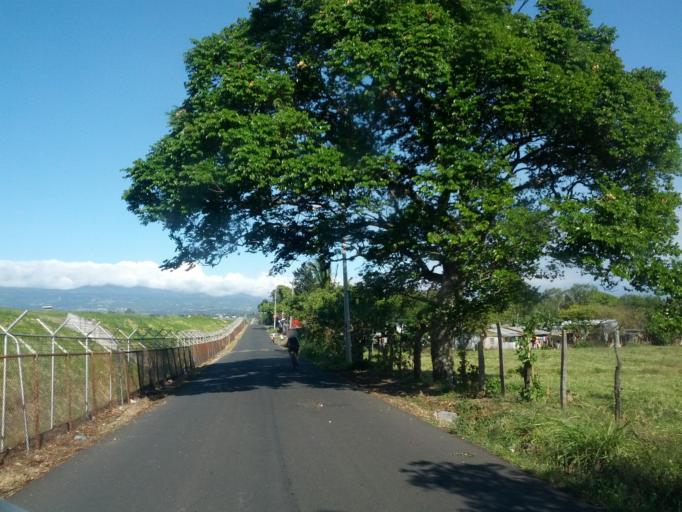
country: CR
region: Alajuela
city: Alajuela
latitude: 9.9908
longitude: -84.2138
